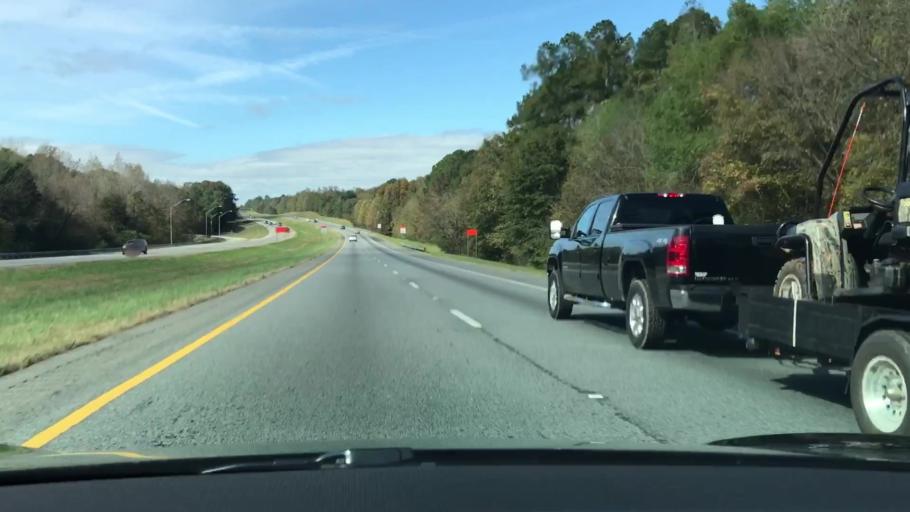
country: US
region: Georgia
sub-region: Walton County
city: Social Circle
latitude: 33.6013
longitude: -83.6549
